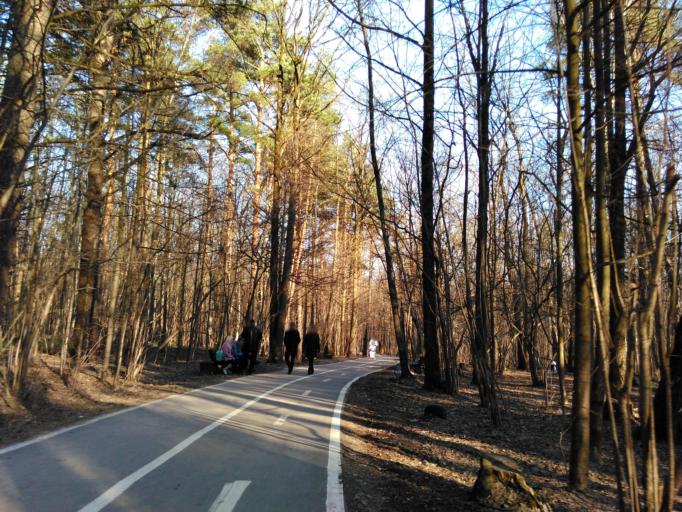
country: RU
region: Moscow
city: Zyuzino
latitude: 55.6327
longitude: 37.5630
